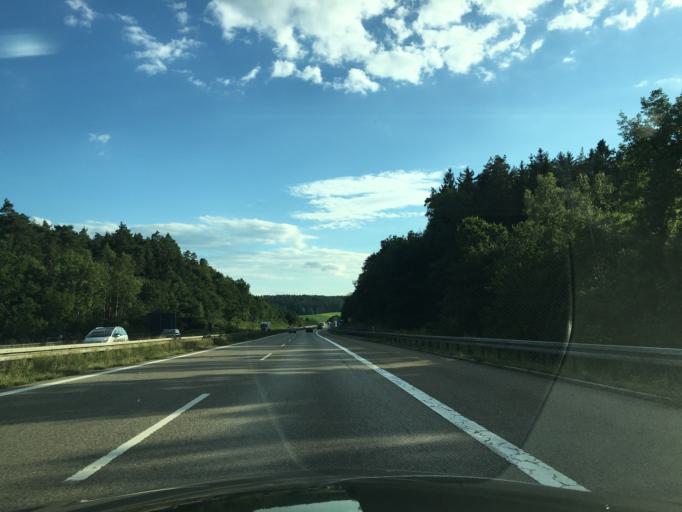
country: DE
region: Bavaria
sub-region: Regierungsbezirk Mittelfranken
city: Petersaurach
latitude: 49.2840
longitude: 10.7252
